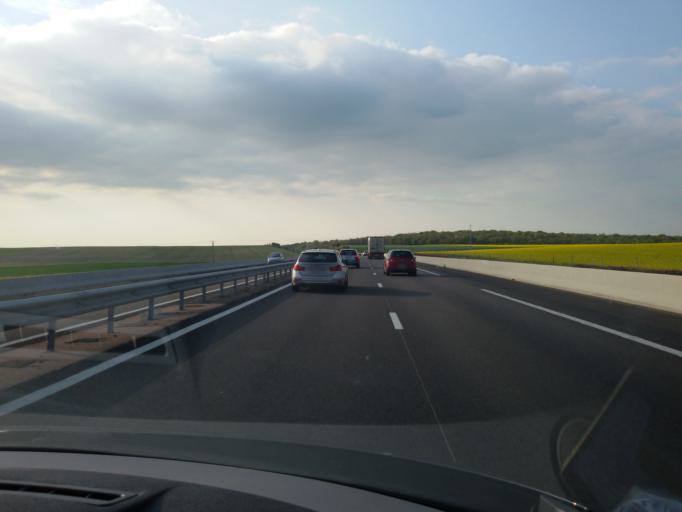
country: FR
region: Champagne-Ardenne
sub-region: Departement de l'Aube
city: Bar-sur-Aube
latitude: 48.1568
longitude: 4.6023
